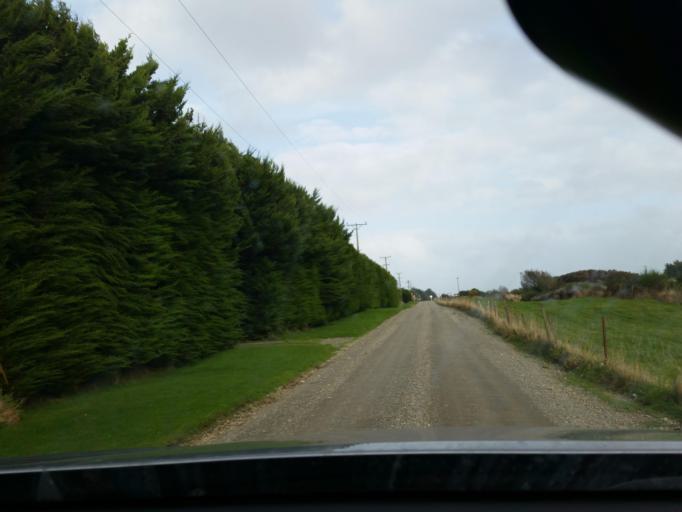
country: NZ
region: Southland
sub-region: Invercargill City
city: Invercargill
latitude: -46.3267
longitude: 168.3406
